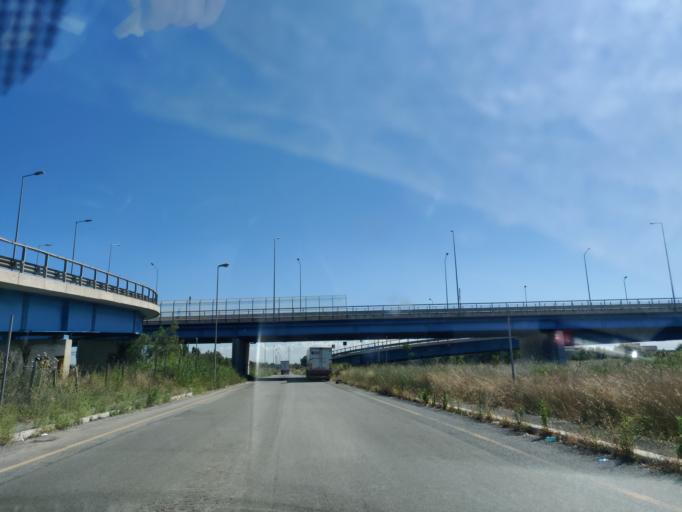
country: IT
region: Latium
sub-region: Citta metropolitana di Roma Capitale
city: Npp 23 (Parco Leonardo)
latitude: 41.8038
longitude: 12.2991
